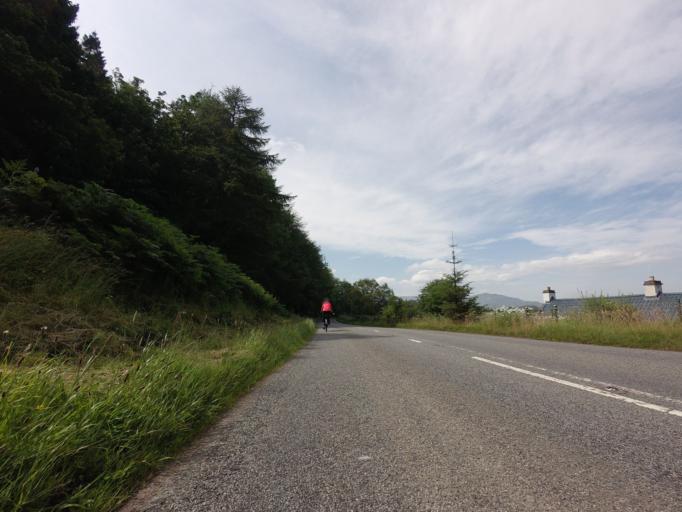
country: GB
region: Scotland
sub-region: Highland
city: Tain
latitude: 57.8268
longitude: -4.1443
